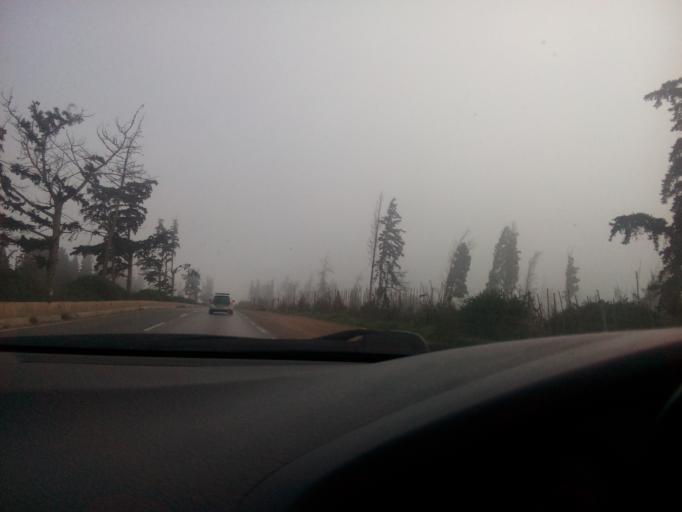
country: DZ
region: Oran
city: Bou Tlelis
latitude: 35.5856
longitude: -0.8144
